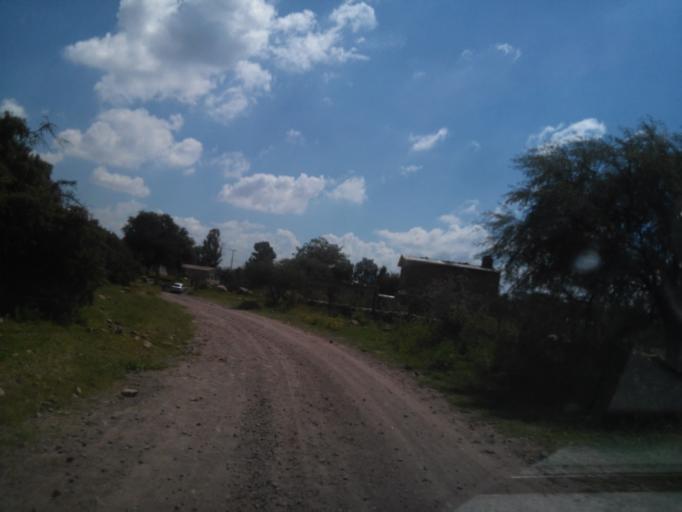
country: MX
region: Durango
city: Victoria de Durango
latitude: 24.0128
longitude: -104.7412
